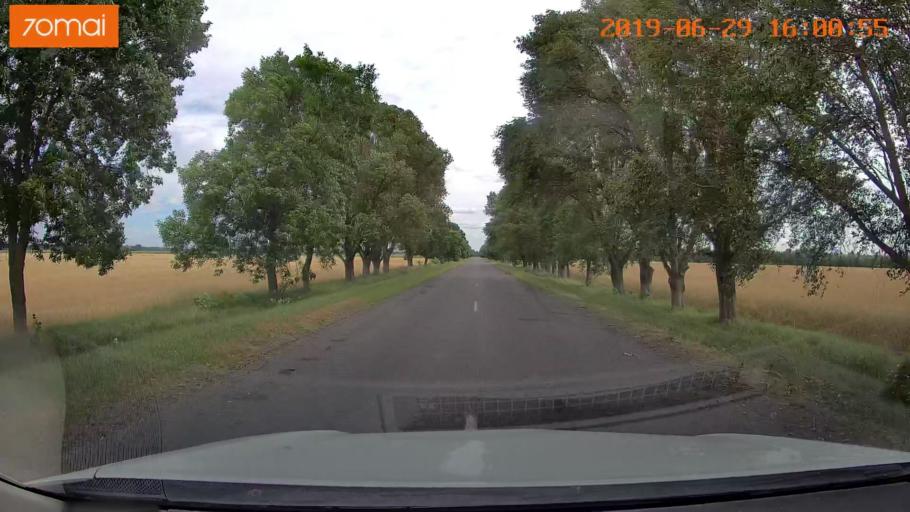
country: BY
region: Brest
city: Luninyets
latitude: 52.2542
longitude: 27.0170
